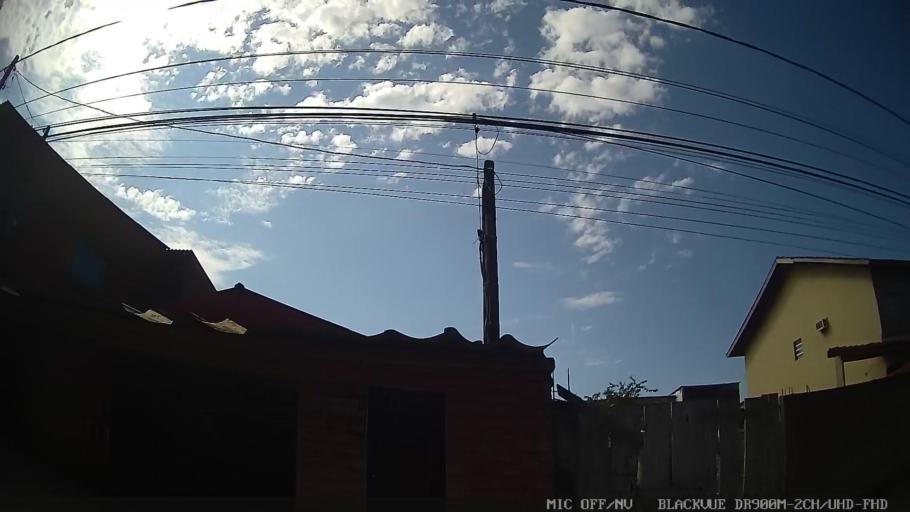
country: BR
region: Sao Paulo
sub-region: Santos
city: Santos
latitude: -23.9389
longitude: -46.2856
